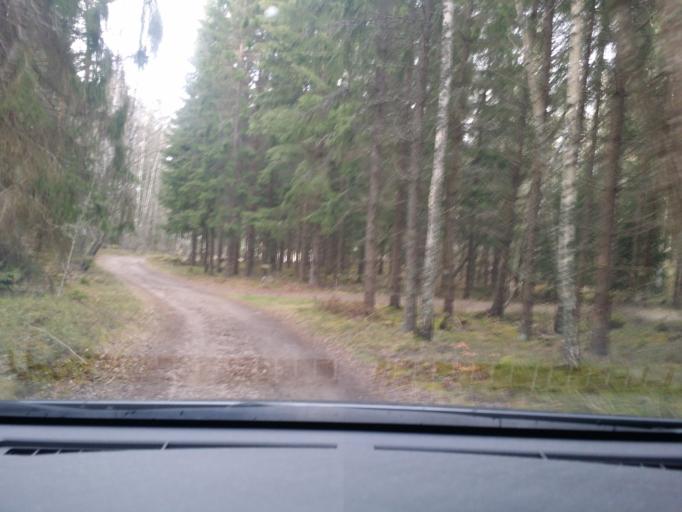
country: SE
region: Soedermanland
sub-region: Eskilstuna Kommun
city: Arla
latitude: 59.3749
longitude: 16.6521
